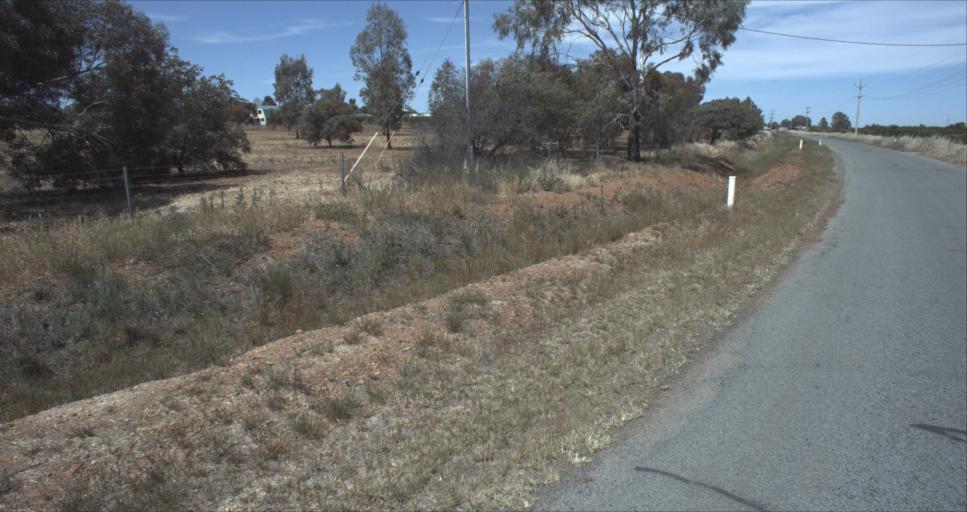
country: AU
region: New South Wales
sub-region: Leeton
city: Leeton
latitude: -34.5829
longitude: 146.4271
